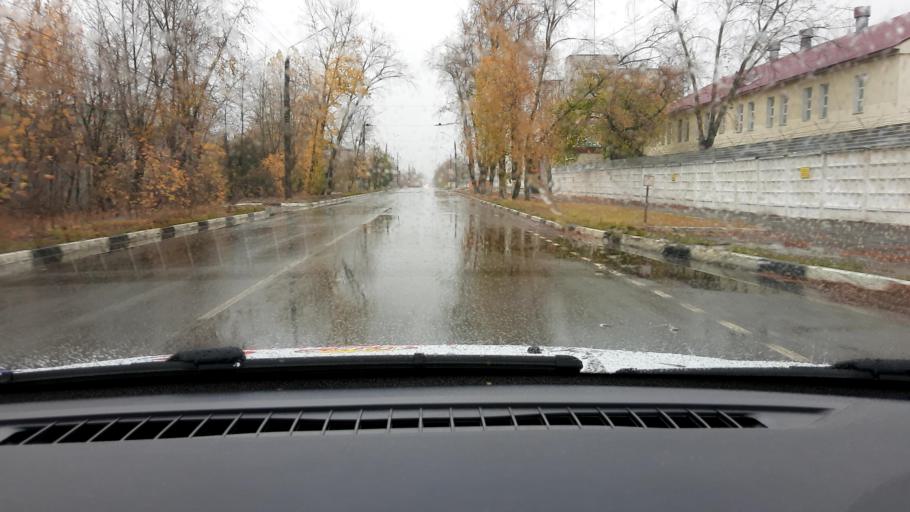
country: RU
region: Nizjnij Novgorod
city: Dzerzhinsk
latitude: 56.2450
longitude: 43.4786
